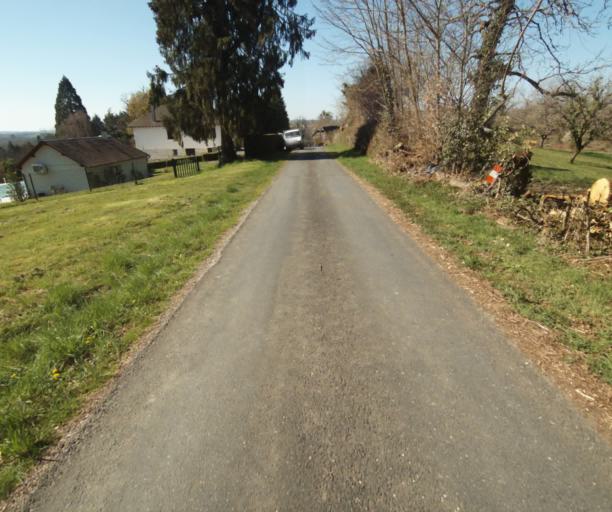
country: FR
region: Limousin
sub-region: Departement de la Correze
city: Saint-Mexant
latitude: 45.3095
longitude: 1.6080
